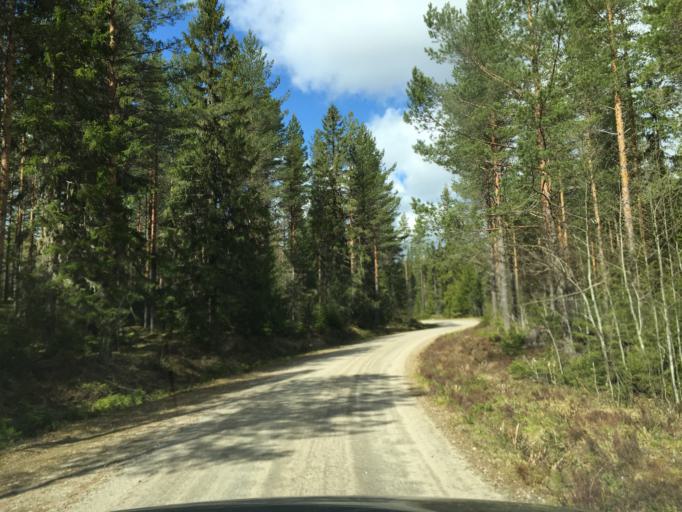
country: SE
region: Gaevleborg
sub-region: Bollnas Kommun
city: Arbra
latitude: 61.5249
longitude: 16.2819
